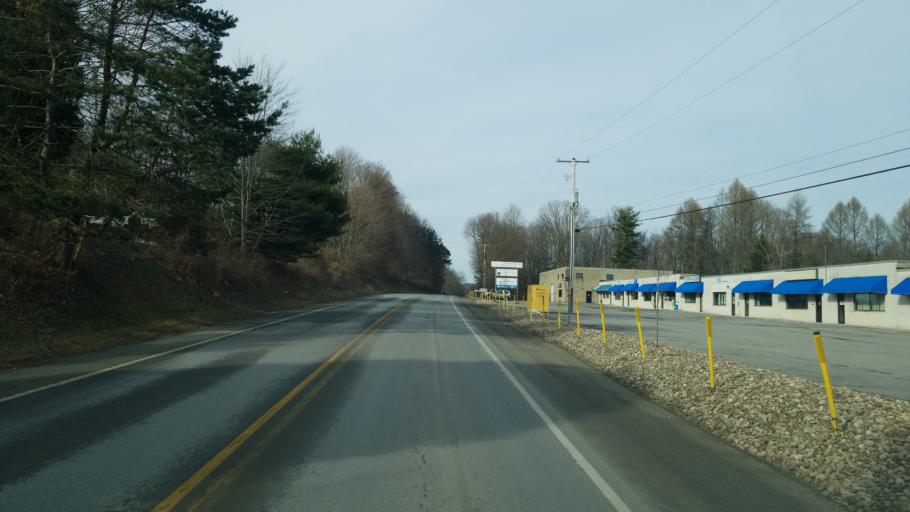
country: US
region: Pennsylvania
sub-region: Jefferson County
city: Punxsutawney
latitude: 40.9624
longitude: -79.0072
